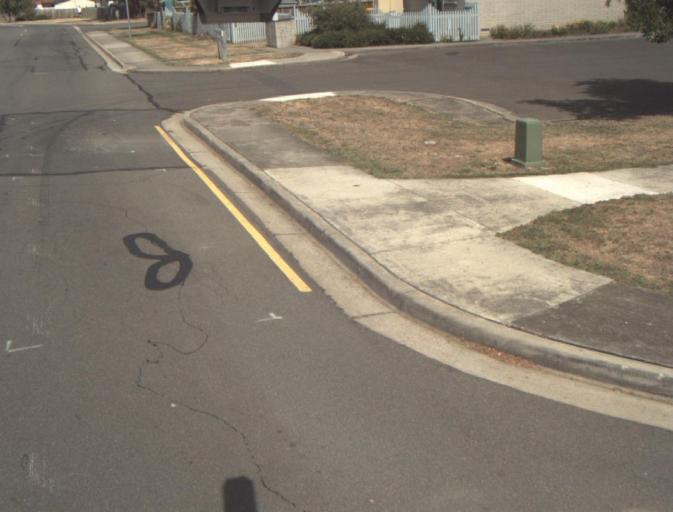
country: AU
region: Tasmania
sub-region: Launceston
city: Newstead
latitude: -41.4170
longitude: 147.1770
